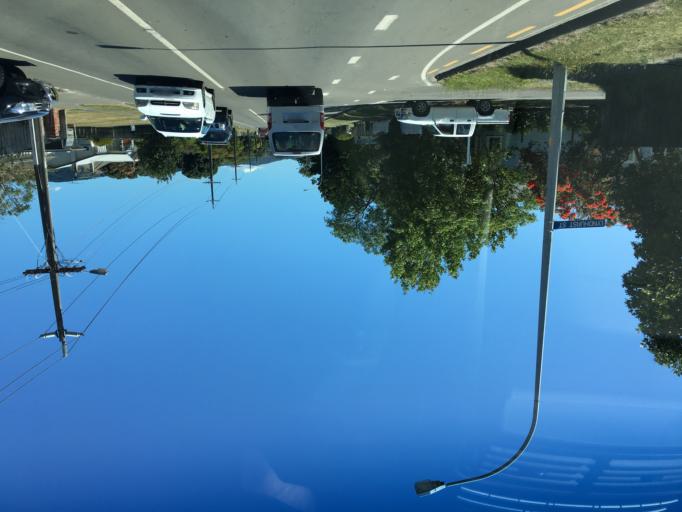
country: NZ
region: Gisborne
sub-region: Gisborne District
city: Gisborne
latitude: -38.6628
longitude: 178.0067
